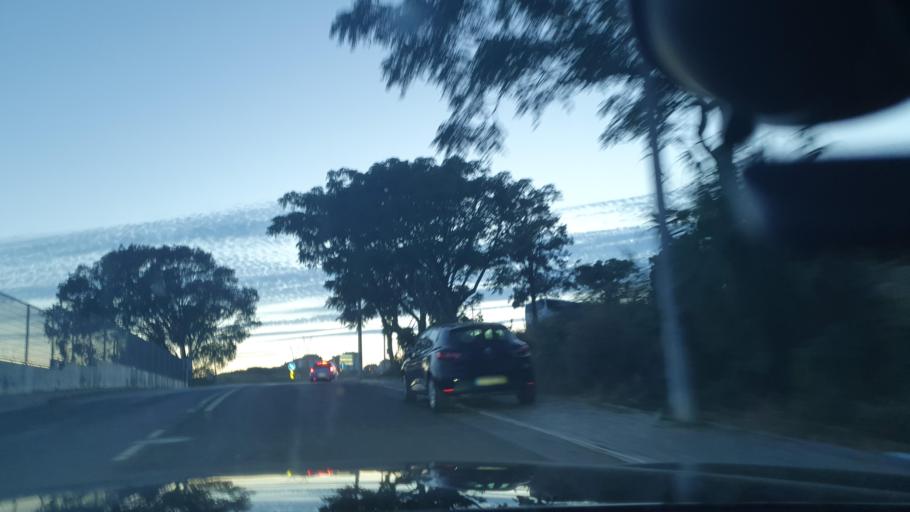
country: PT
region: Lisbon
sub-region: Sintra
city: Queluz
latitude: 38.7616
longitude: -9.2651
